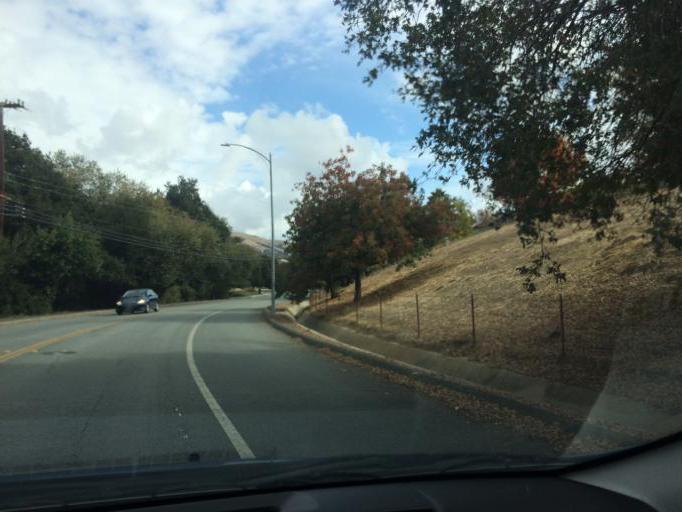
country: US
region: California
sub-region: Santa Clara County
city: Seven Trees
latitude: 37.2796
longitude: -121.7554
